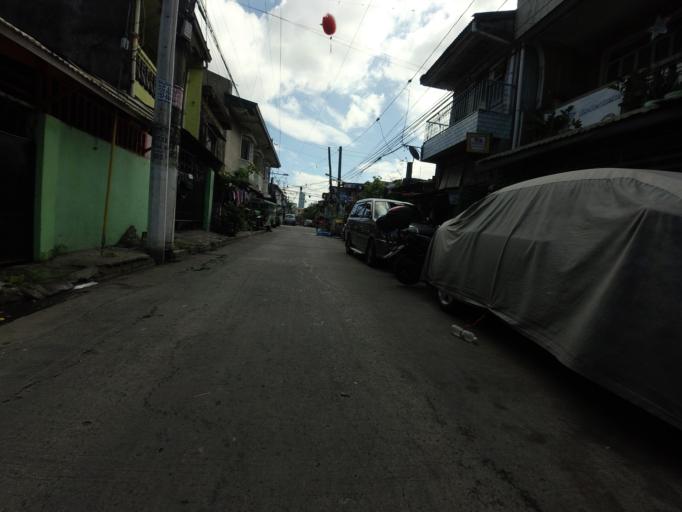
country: PH
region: Metro Manila
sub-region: City of Manila
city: Quiapo
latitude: 14.5748
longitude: 121.0066
